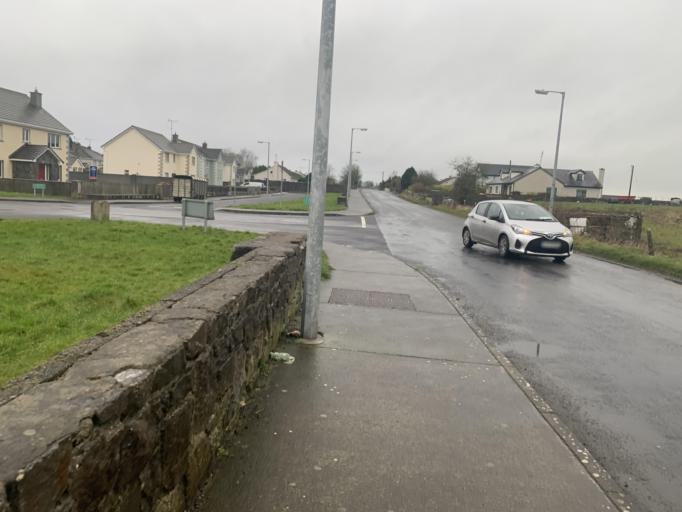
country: IE
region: Connaught
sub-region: County Galway
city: Tuam
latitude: 53.5314
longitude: -8.8542
